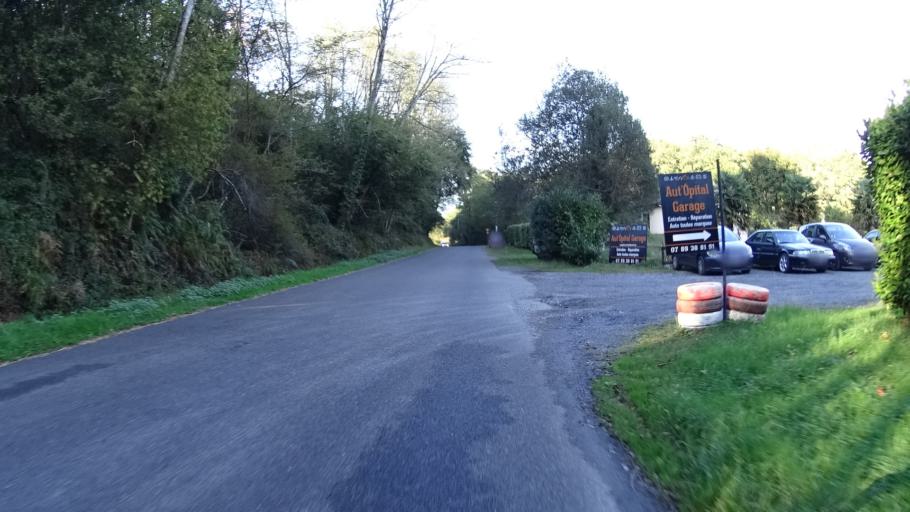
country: FR
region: Aquitaine
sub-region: Departement des Landes
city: Saint-Paul-les-Dax
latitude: 43.7367
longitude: -1.0436
